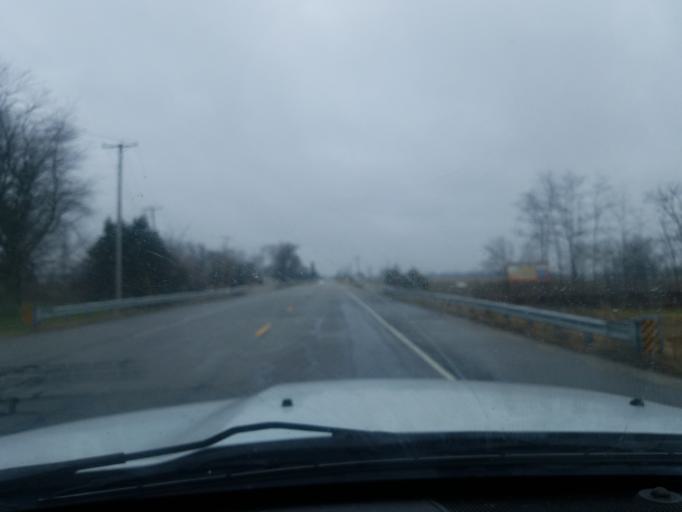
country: US
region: Indiana
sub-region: Wells County
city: Ossian
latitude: 40.9377
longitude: -85.1675
